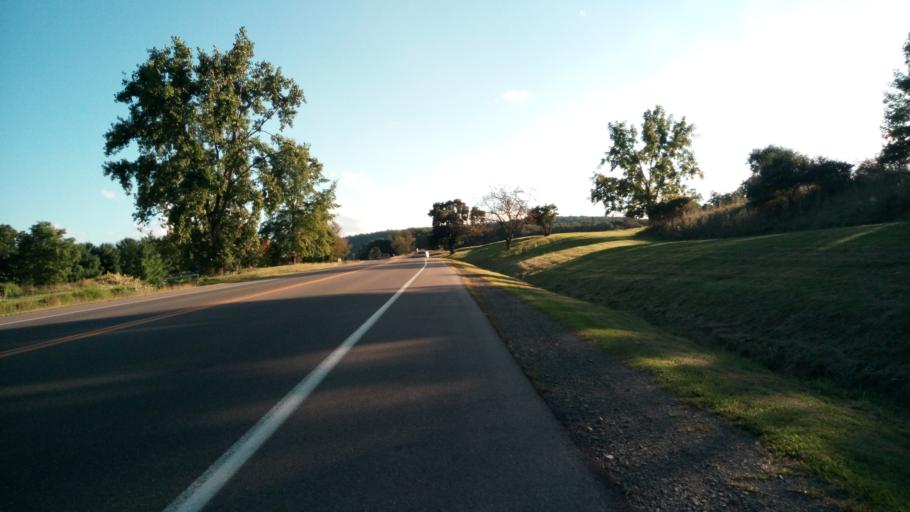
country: US
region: New York
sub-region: Chemung County
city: Elmira Heights
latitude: 42.1130
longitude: -76.8285
